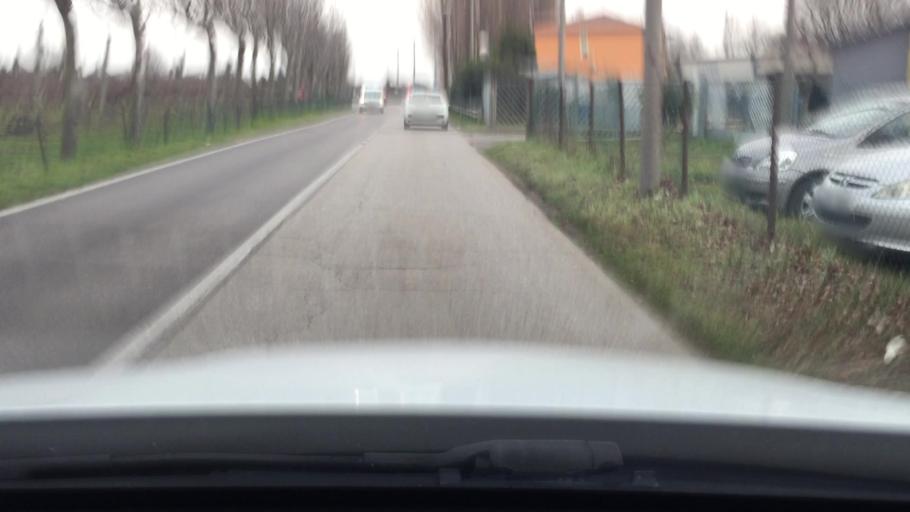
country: IT
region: Veneto
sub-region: Provincia di Verona
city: San Giovanni Lupatoto
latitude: 45.3794
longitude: 11.0231
